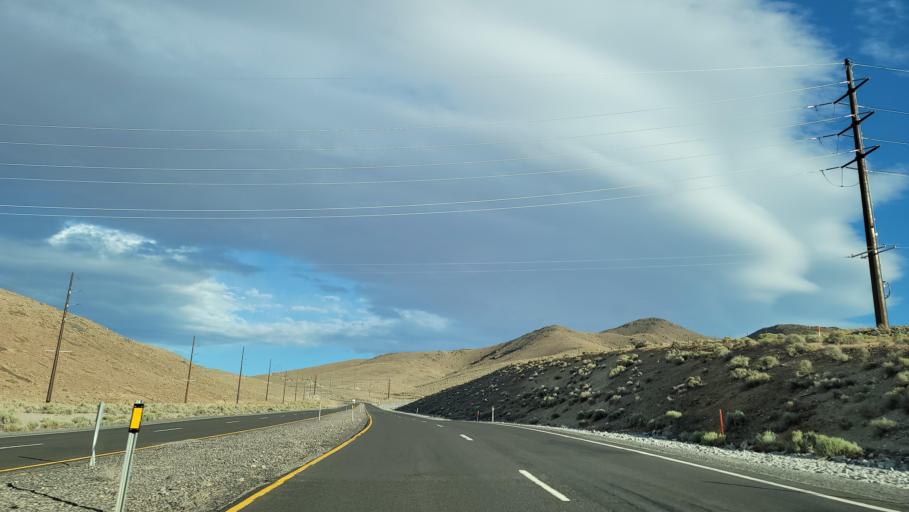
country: US
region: Nevada
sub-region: Lyon County
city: Stagecoach
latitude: 39.5193
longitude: -119.4739
